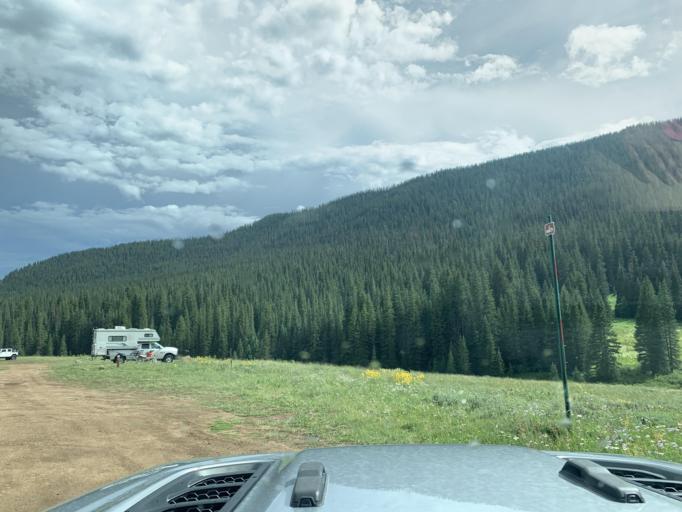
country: US
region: Colorado
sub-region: Gunnison County
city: Crested Butte
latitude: 38.9340
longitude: -107.0187
